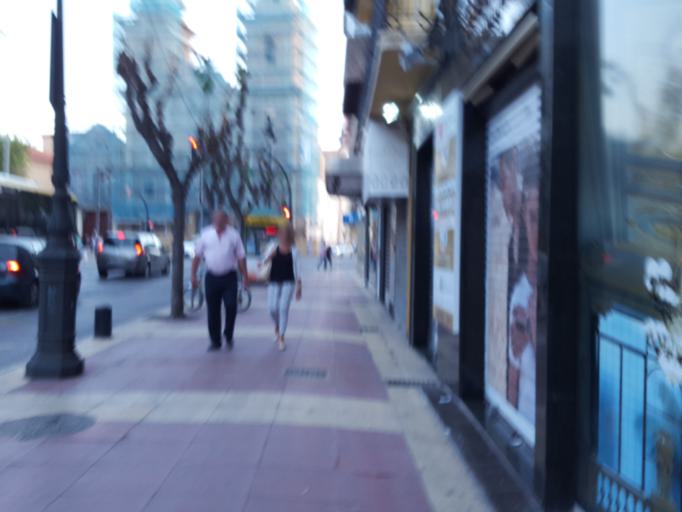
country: ES
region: Murcia
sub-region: Murcia
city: Murcia
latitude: 37.9802
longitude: -1.1303
